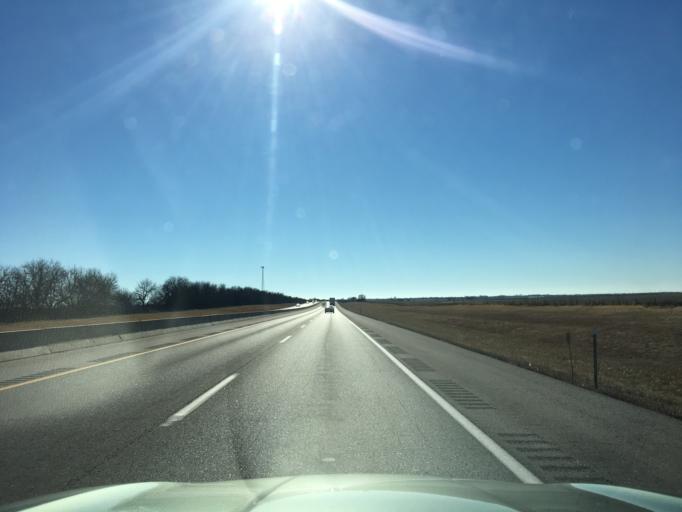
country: US
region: Kansas
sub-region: Sumner County
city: Wellington
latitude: 37.1260
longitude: -97.3390
